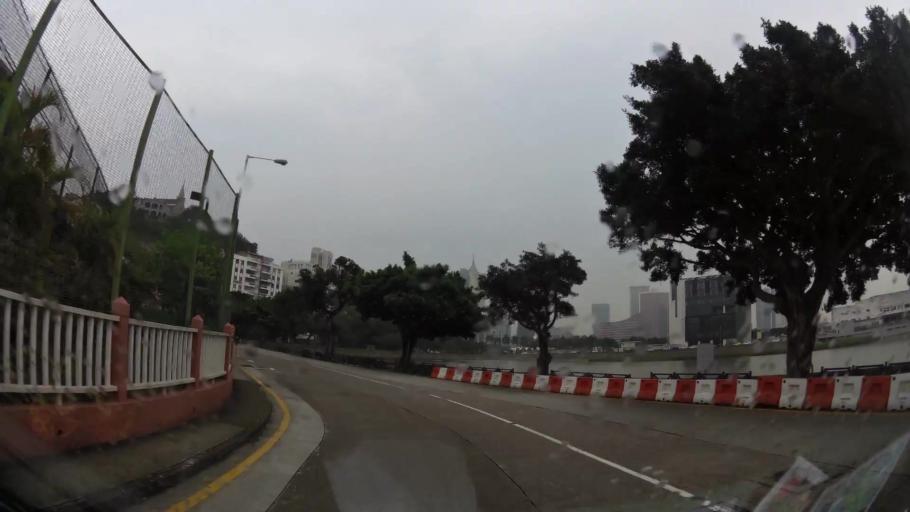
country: CN
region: Guangdong
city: Wanzai
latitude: 22.1843
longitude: 113.5347
